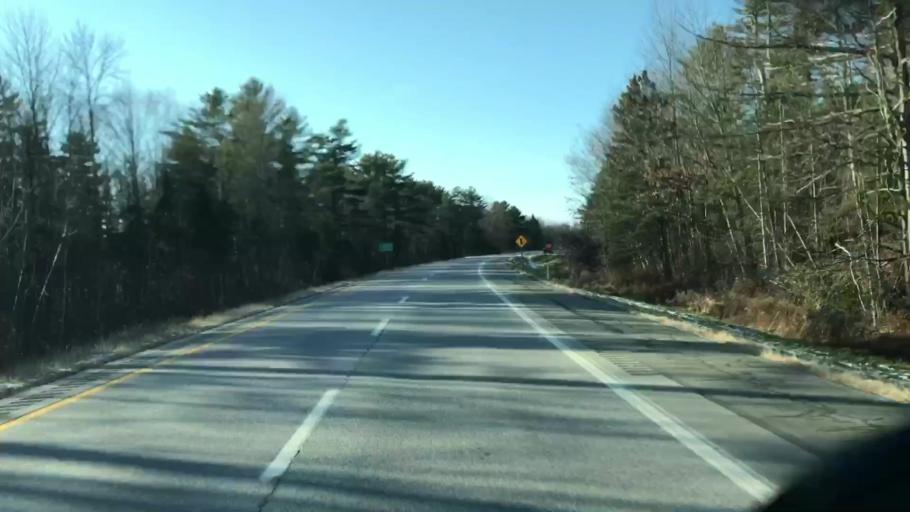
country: US
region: Maine
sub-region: Penobscot County
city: Hermon
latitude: 44.7592
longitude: -68.9759
